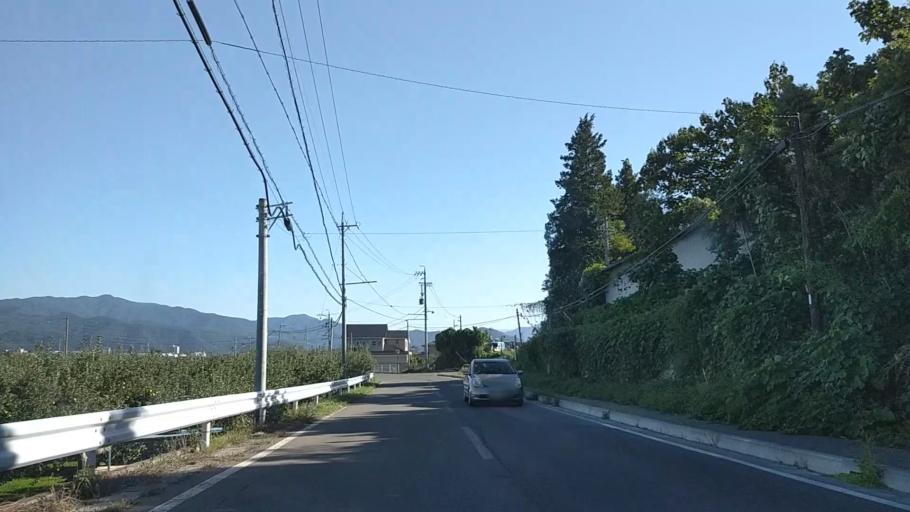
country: JP
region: Nagano
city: Nagano-shi
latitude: 36.5945
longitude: 138.1326
